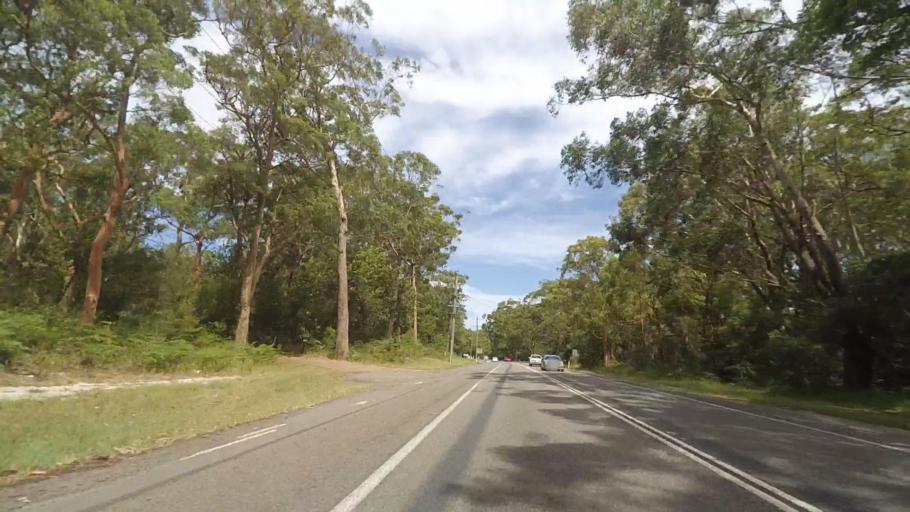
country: AU
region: New South Wales
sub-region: Port Stephens Shire
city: Medowie
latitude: -32.7919
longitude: 151.9402
